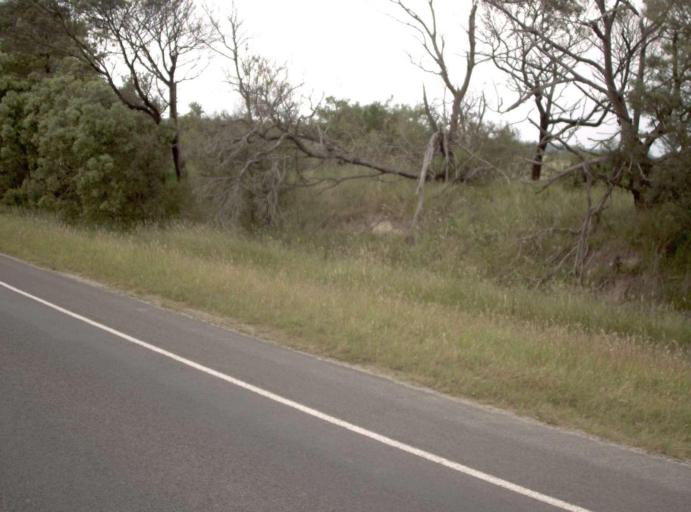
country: AU
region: Victoria
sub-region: Cardinia
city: Koo-Wee-Rup
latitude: -38.3064
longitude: 145.5722
